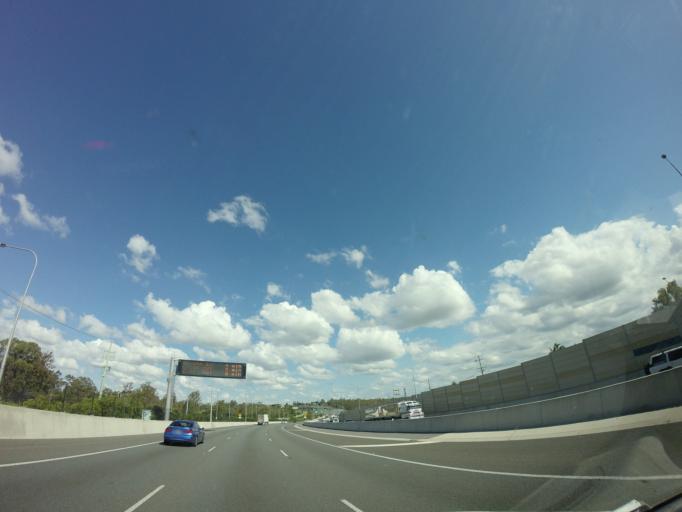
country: AU
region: Queensland
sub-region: Ipswich
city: Riverview
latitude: -27.5981
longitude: 152.8549
